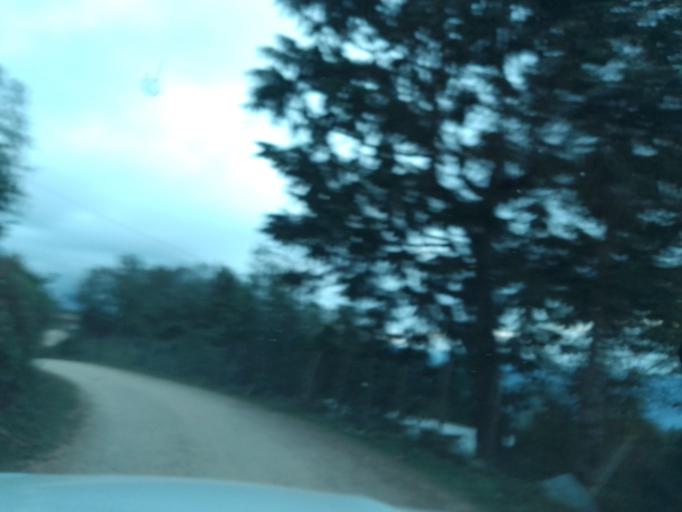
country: MX
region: Chiapas
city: Motozintla de Mendoza
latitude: 15.2296
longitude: -92.2368
